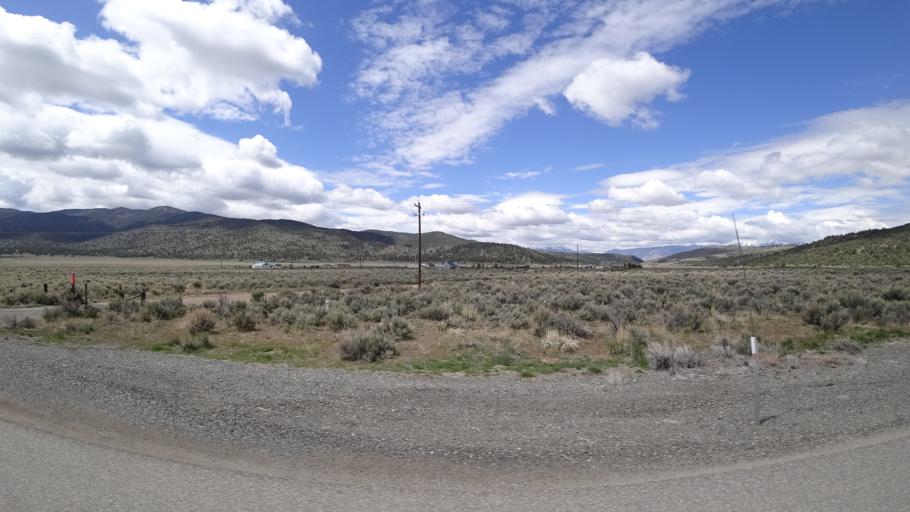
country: US
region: Nevada
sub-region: Douglas County
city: Gardnerville Ranchos
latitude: 38.7991
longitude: -119.6035
